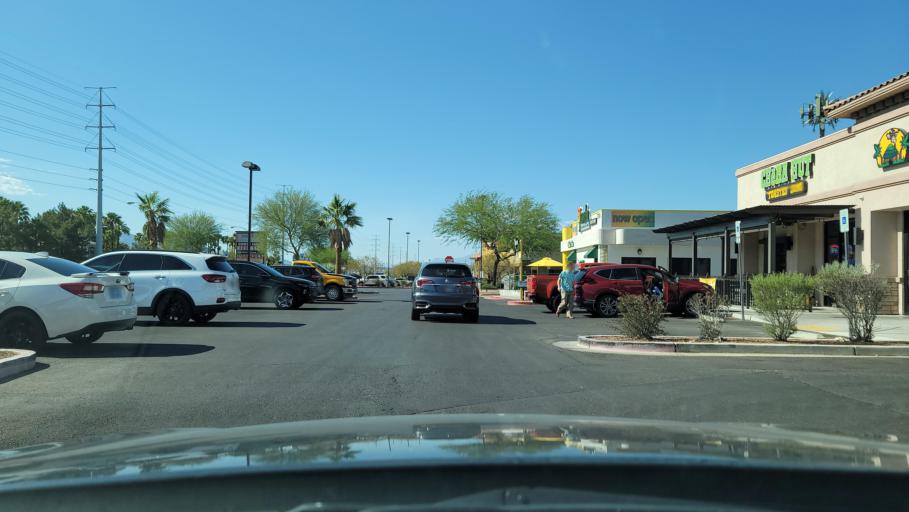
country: US
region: Nevada
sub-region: Clark County
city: Enterprise
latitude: 36.0568
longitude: -115.2787
